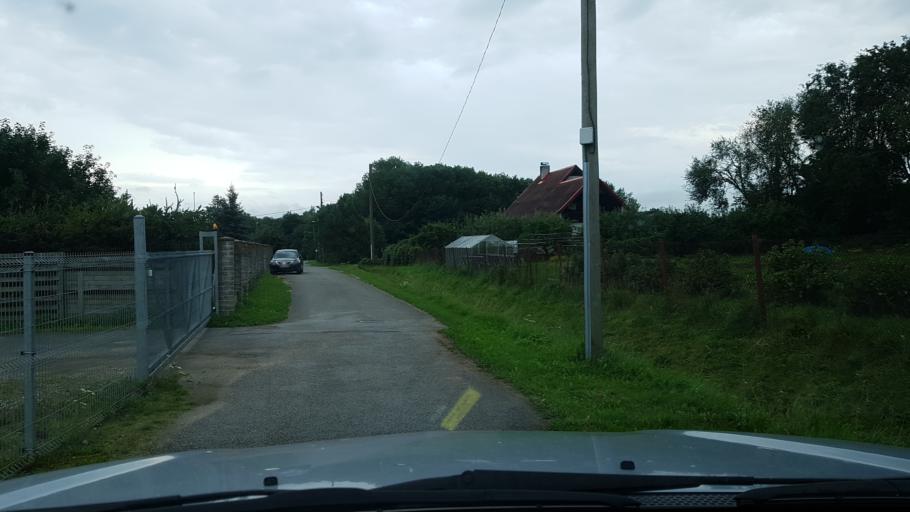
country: EE
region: Harju
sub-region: Rae vald
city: Jueri
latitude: 59.3534
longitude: 24.9054
